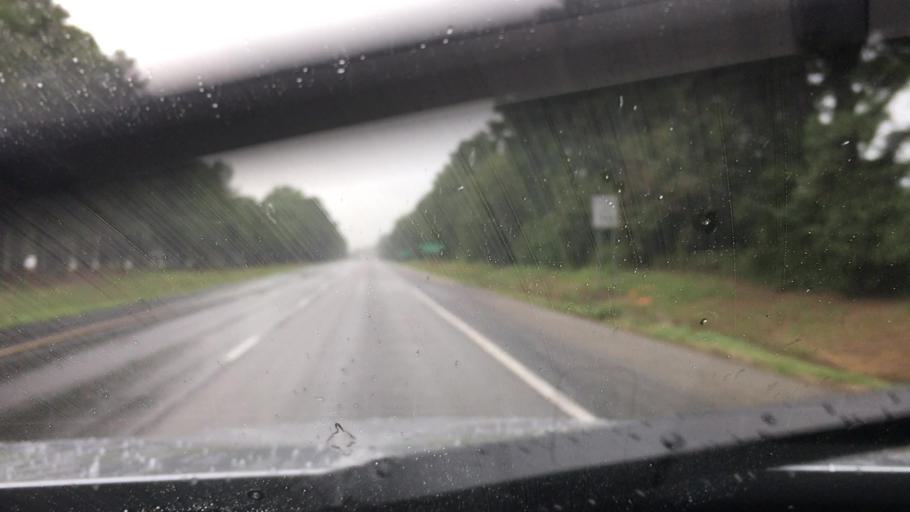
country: US
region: North Carolina
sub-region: Northampton County
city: Gaston
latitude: 36.5173
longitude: -77.5878
